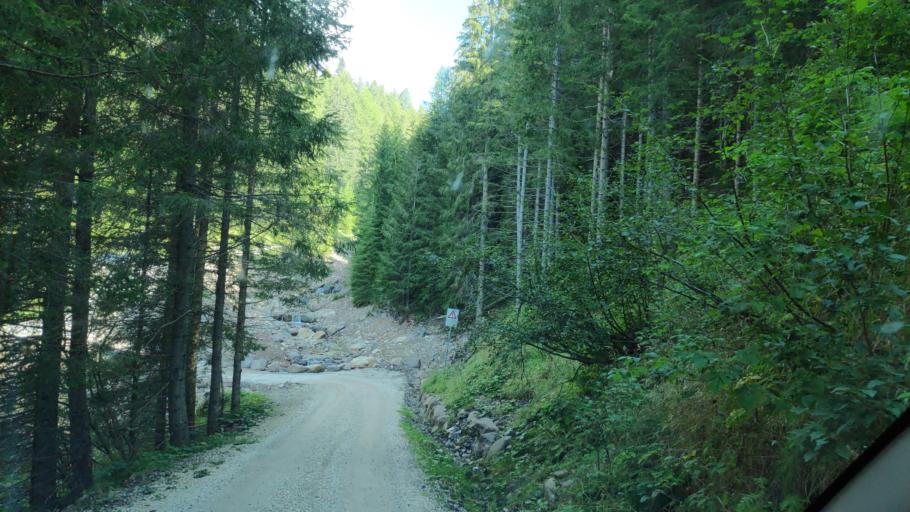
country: IT
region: Trentino-Alto Adige
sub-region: Provincia di Trento
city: Moena
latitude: 46.3202
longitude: 11.6883
